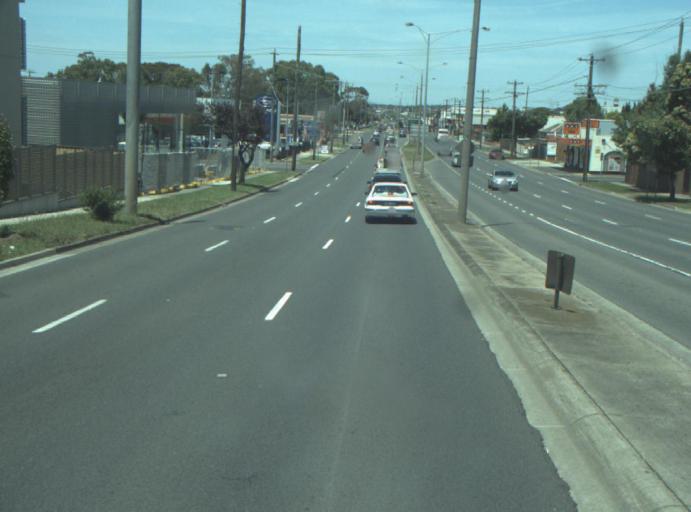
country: AU
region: Victoria
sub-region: Greater Geelong
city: Geelong
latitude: -38.1519
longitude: 144.3519
